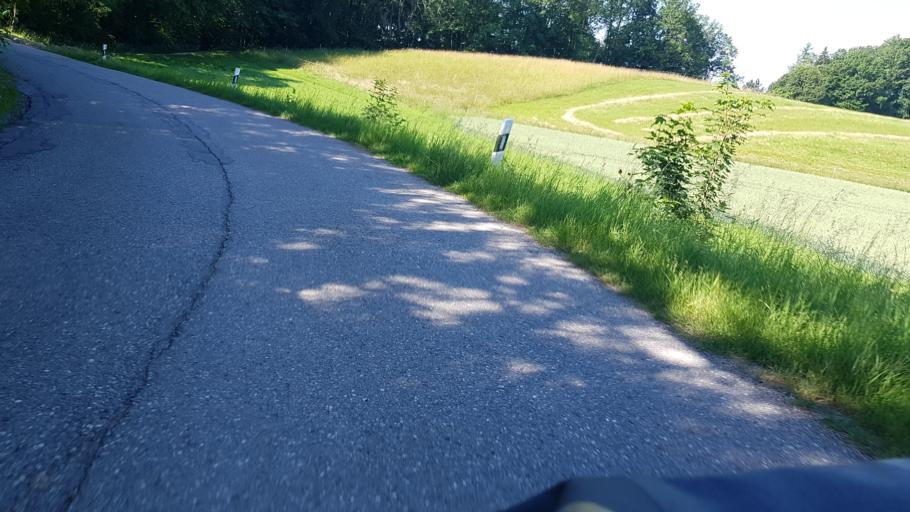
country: DE
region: Bavaria
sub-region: Upper Bavaria
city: Gauting
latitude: 48.0319
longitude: 11.3755
